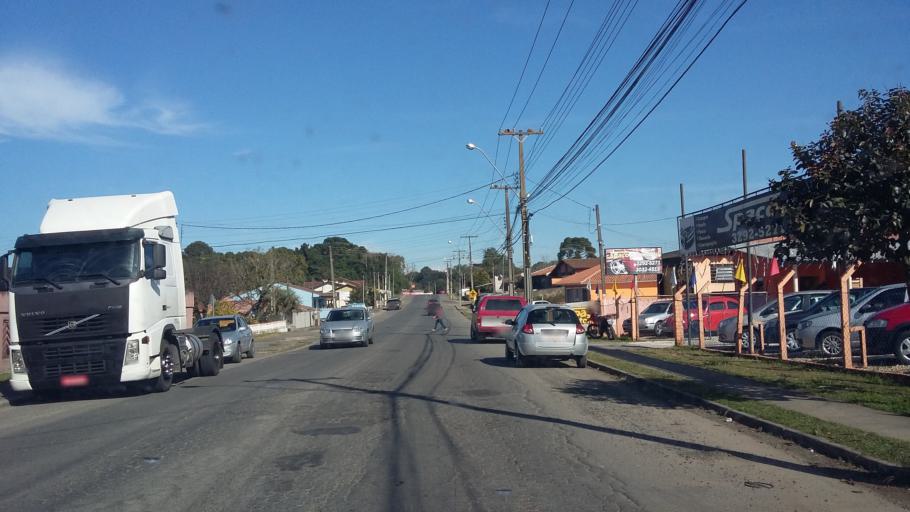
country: BR
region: Parana
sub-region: Campo Largo
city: Campo Largo
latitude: -25.4575
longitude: -49.5445
